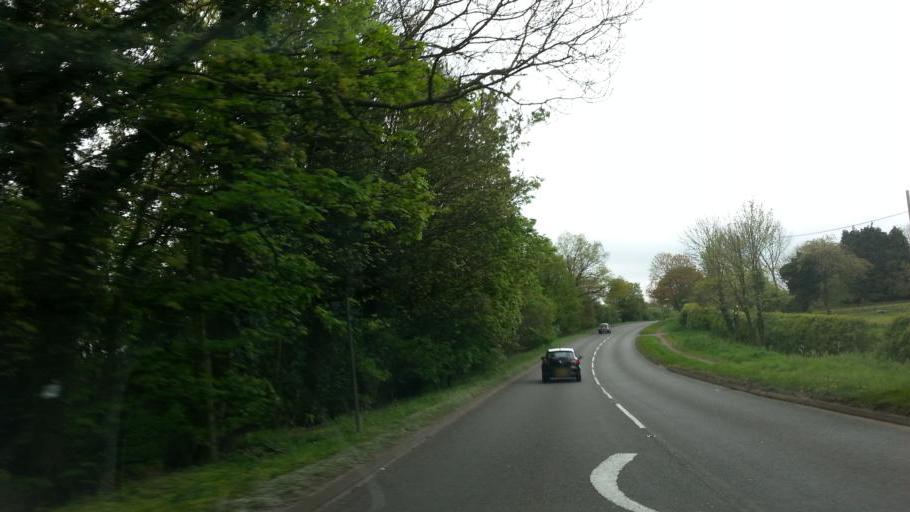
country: GB
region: England
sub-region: Leicestershire
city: Lutterworth
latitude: 52.4461
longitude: -1.1961
